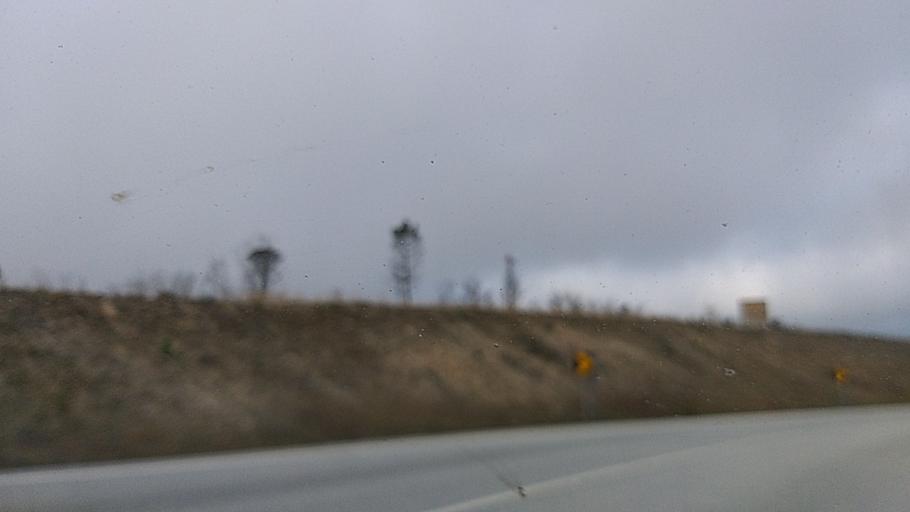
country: PT
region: Guarda
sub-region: Fornos de Algodres
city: Fornos de Algodres
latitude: 40.7010
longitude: -7.4845
